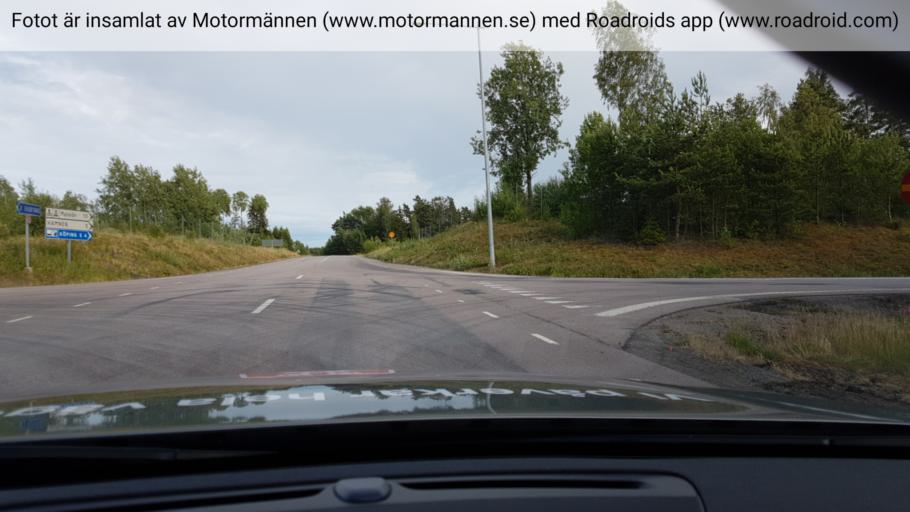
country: SE
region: Vaestmanland
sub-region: Kopings Kommun
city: Koping
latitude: 59.4999
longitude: 15.9345
